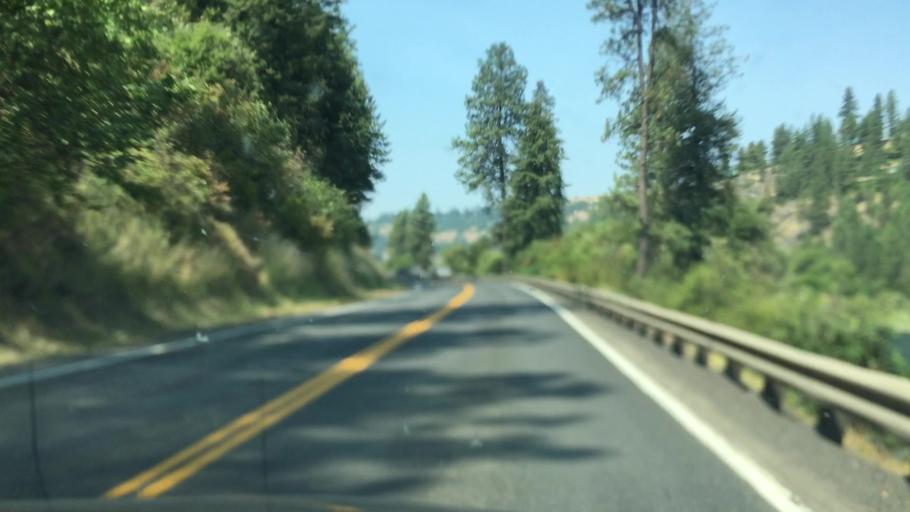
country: US
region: Idaho
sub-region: Clearwater County
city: Orofino
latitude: 46.4972
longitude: -116.4157
